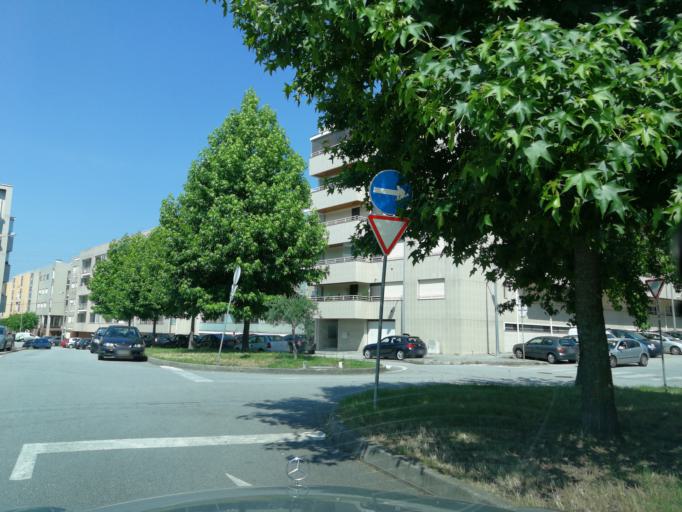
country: PT
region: Braga
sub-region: Braga
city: Adaufe
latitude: 41.5633
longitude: -8.3904
